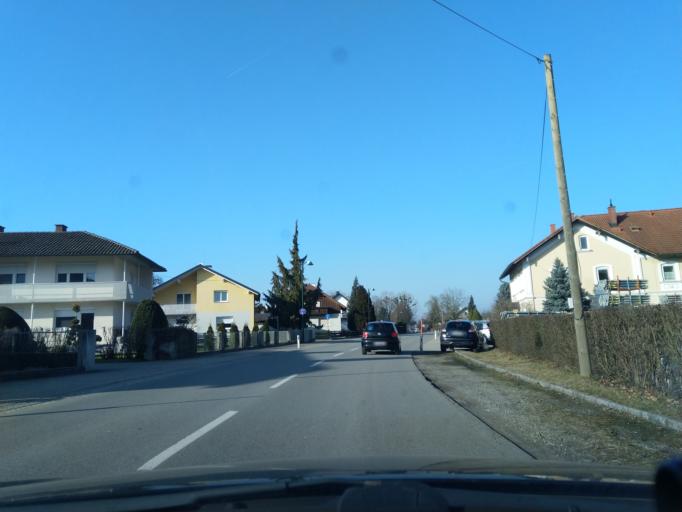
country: AT
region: Upper Austria
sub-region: Politischer Bezirk Scharding
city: Sankt Marienkirchen bei Schaerding
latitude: 48.2961
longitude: 13.4326
